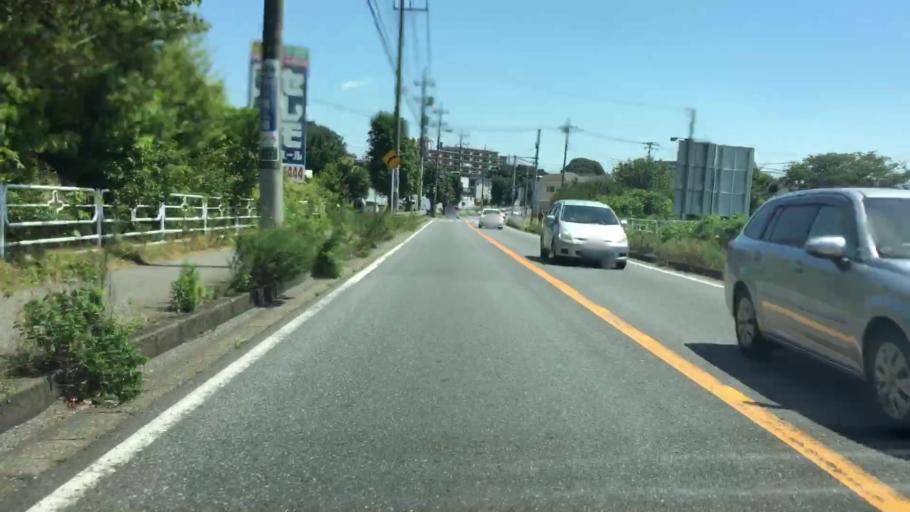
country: JP
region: Chiba
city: Funabashi
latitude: 35.7360
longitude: 139.9564
